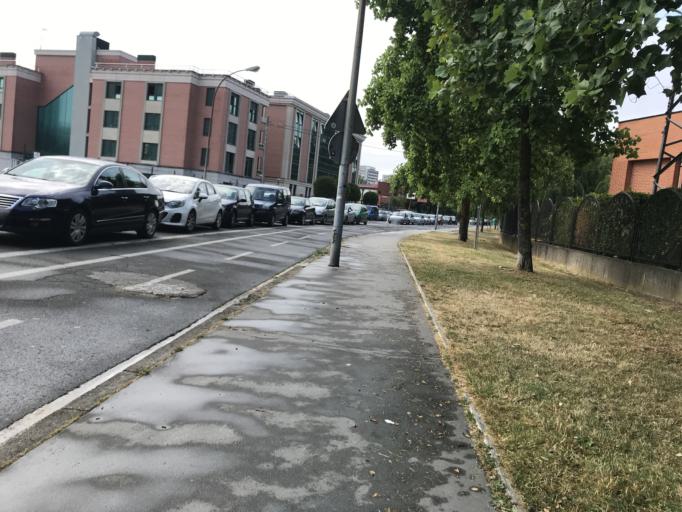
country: ES
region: Basque Country
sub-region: Provincia de Alava
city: Gasteiz / Vitoria
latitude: 42.8393
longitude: -2.6630
